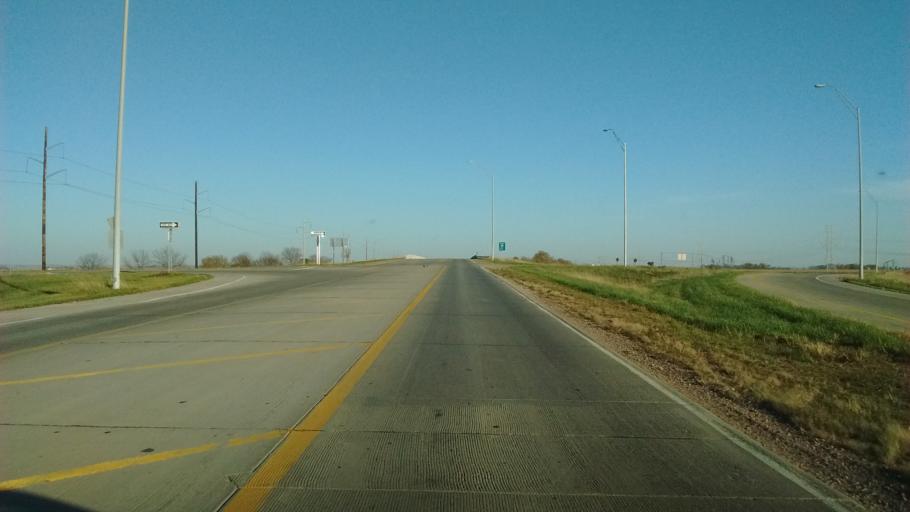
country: US
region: Iowa
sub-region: Woodbury County
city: Sergeant Bluff
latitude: 42.3299
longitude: -96.3218
